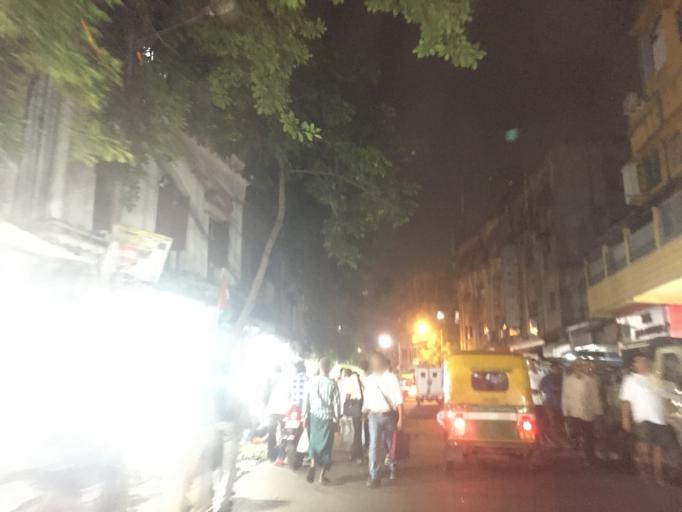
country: IN
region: West Bengal
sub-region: Kolkata
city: Bara Bazar
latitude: 22.5622
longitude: 88.3553
